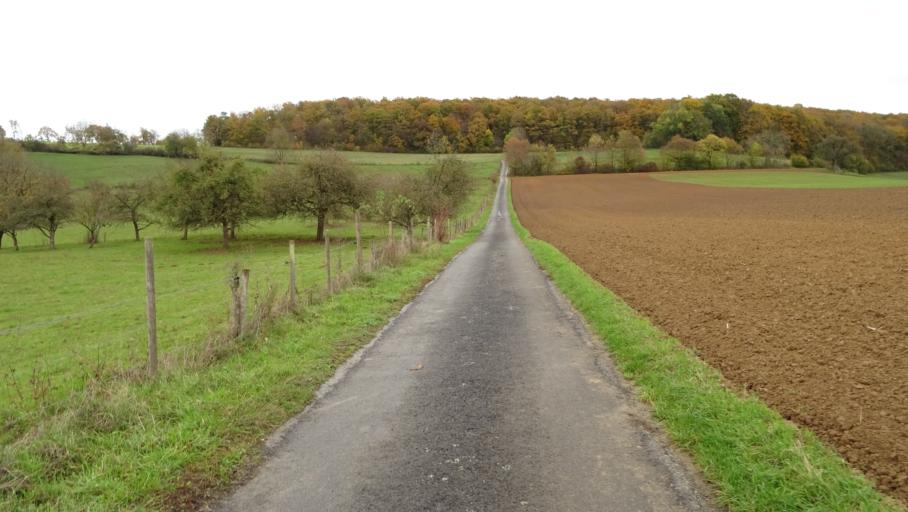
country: DE
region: Baden-Wuerttemberg
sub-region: Karlsruhe Region
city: Obrigheim
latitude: 49.3731
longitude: 9.0900
